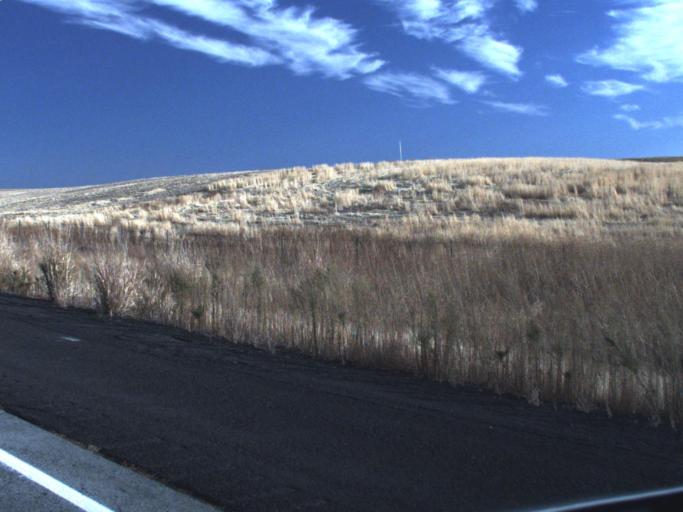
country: US
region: Washington
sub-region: Adams County
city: Ritzville
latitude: 47.0922
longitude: -118.4095
